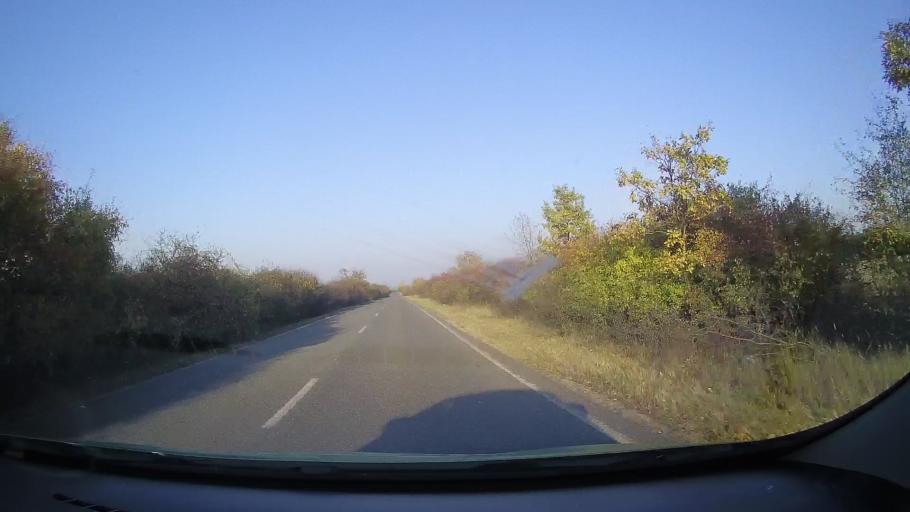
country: RO
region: Arad
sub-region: Comuna Tarnova
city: Chier
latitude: 46.3254
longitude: 21.8336
